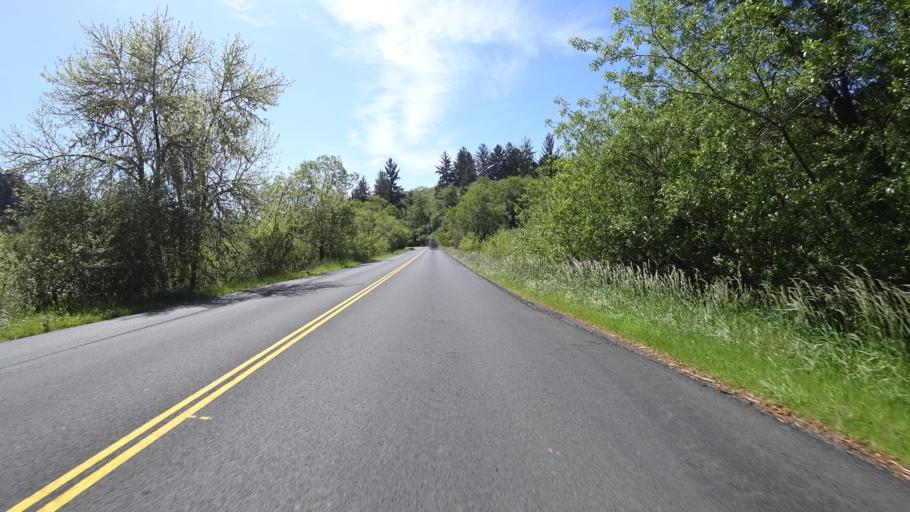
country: US
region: California
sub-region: Humboldt County
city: Westhaven-Moonstone
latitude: 41.3079
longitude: -124.0454
